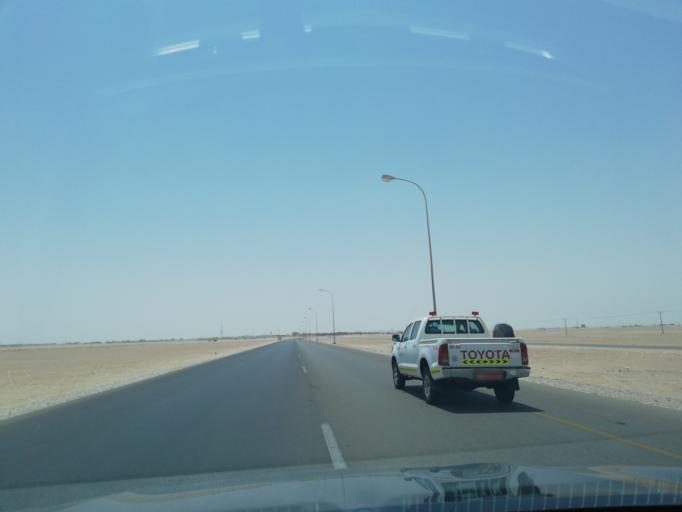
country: OM
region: Al Wusta
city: Hayma'
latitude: 19.9718
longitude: 56.3012
